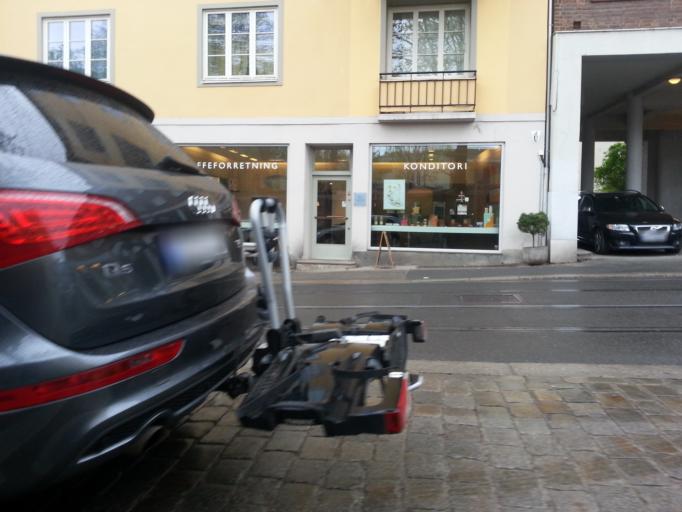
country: NO
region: Oslo
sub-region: Oslo
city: Oslo
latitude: 59.9196
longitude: 10.7186
